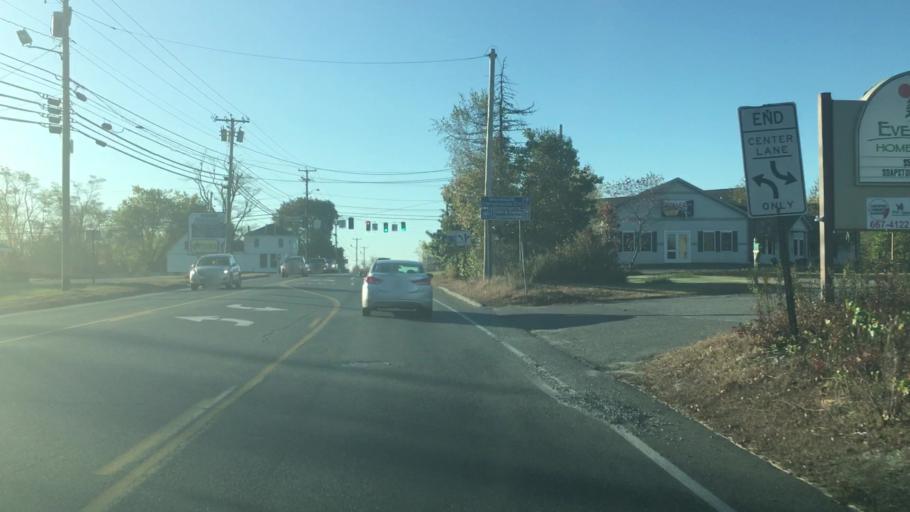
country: US
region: Maine
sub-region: Hancock County
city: Ellsworth
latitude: 44.5203
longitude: -68.3963
